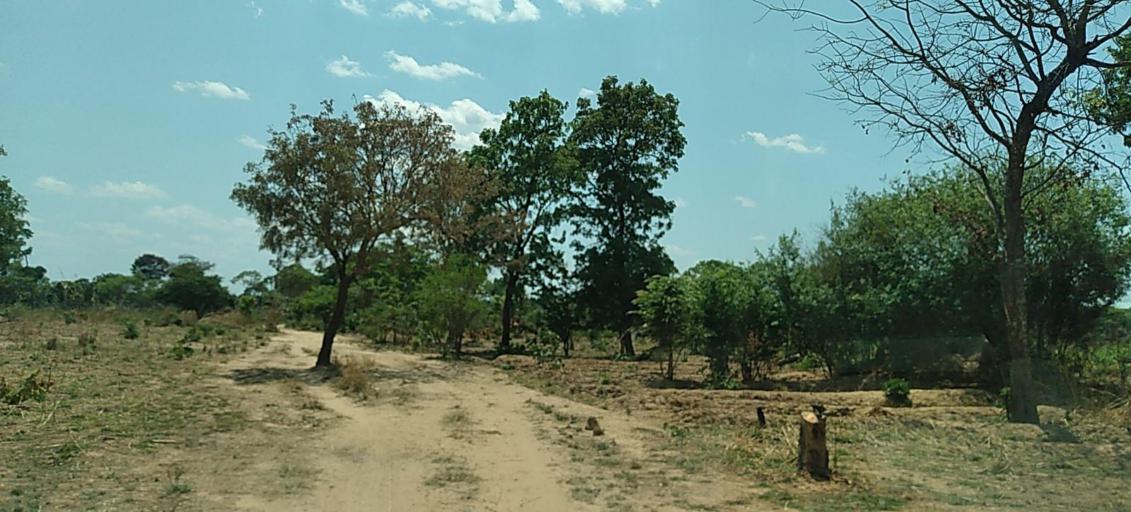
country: ZM
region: Central
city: Kapiri Mposhi
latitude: -13.6347
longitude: 28.7508
